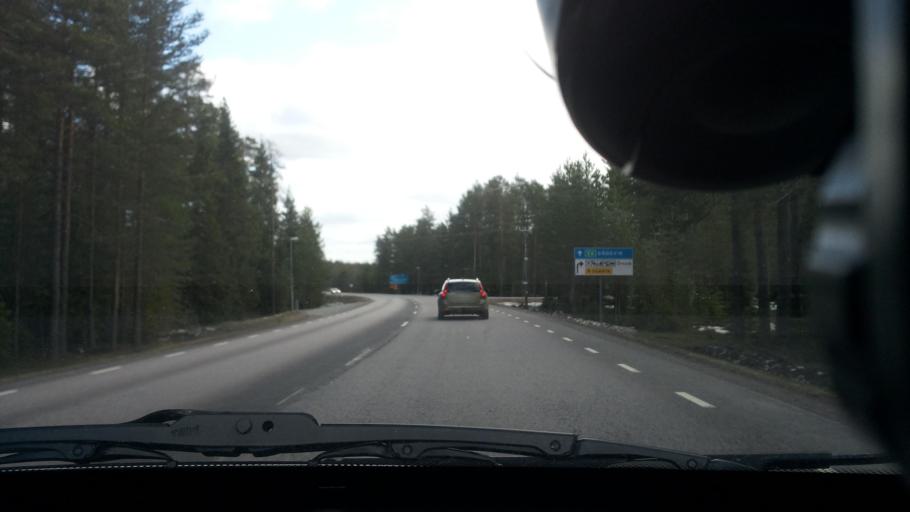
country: SE
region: Norrbotten
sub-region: Lulea Kommun
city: Gammelstad
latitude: 65.6019
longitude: 22.0376
